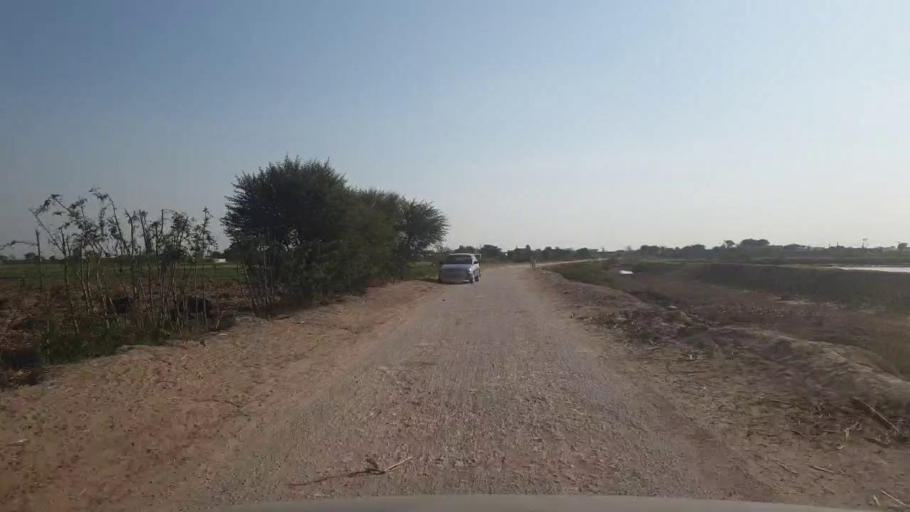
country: PK
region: Sindh
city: Chambar
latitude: 25.2926
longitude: 68.8535
